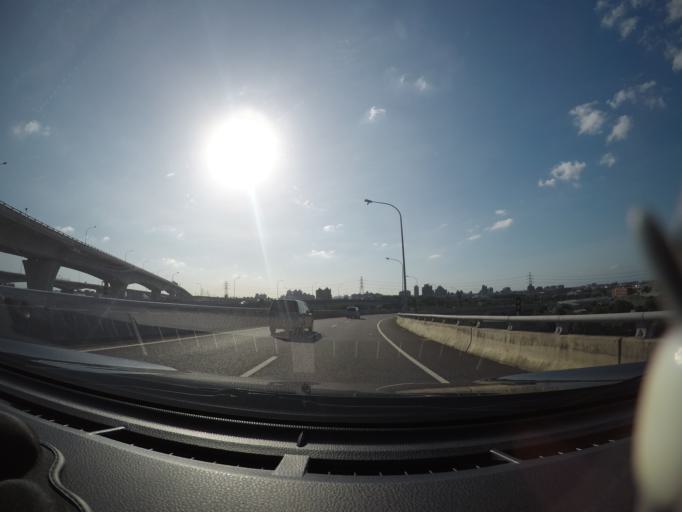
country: TW
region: Taiwan
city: Taoyuan City
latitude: 25.0209
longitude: 121.2734
